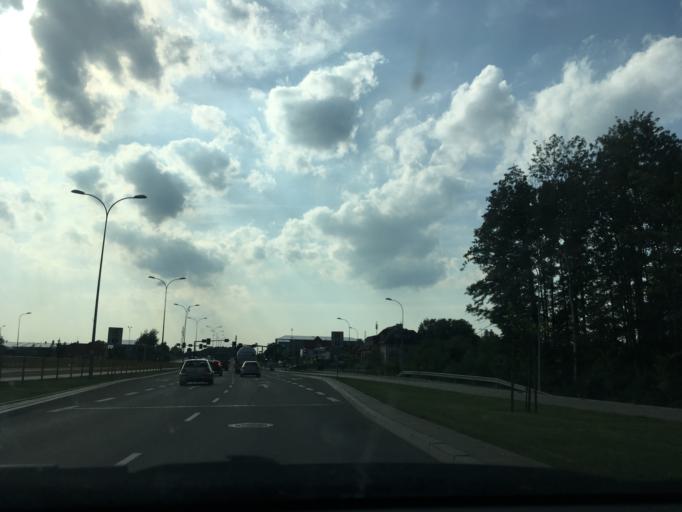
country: PL
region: Podlasie
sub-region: Bialystok
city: Bialystok
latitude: 53.1387
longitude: 23.2146
